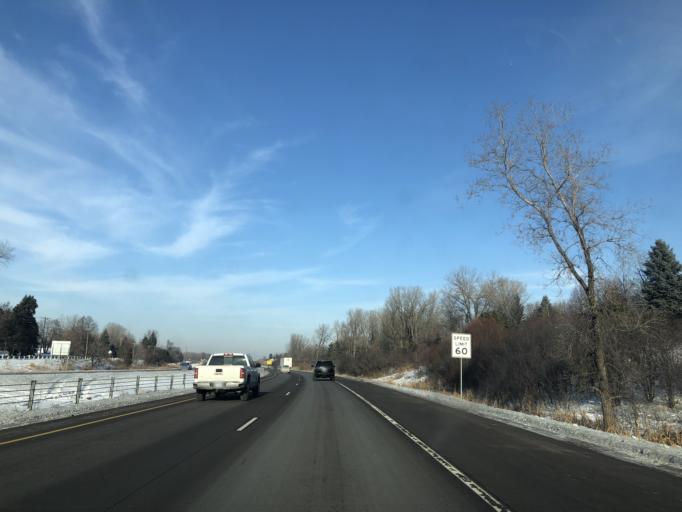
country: US
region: Minnesota
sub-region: Ramsey County
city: Shoreview
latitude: 45.0741
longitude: -93.1701
